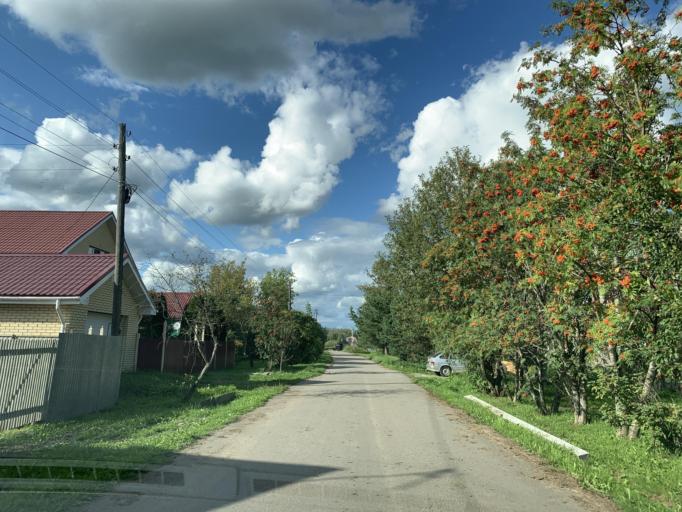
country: RU
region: Jaroslavl
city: Tunoshna
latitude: 57.6640
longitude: 40.0716
